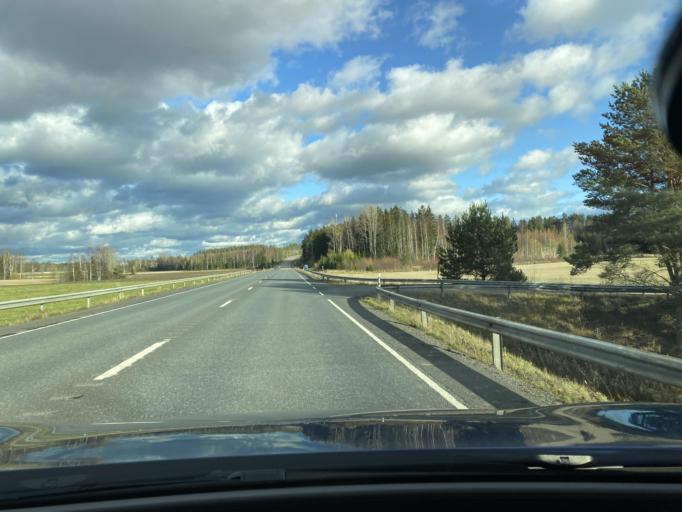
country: FI
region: Haeme
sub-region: Riihimaeki
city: Hausjaervi
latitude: 60.7876
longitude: 24.9338
